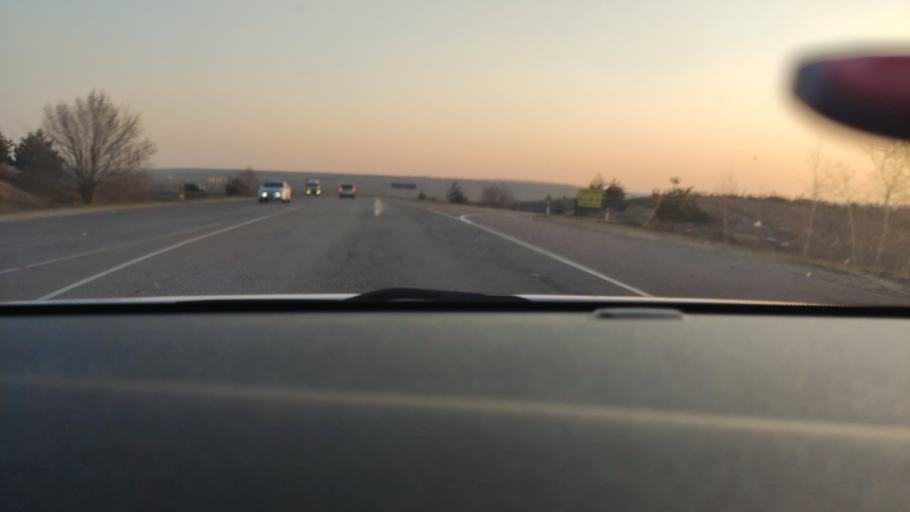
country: RU
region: Voronezj
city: Kolodeznyy
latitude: 51.3563
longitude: 39.1772
